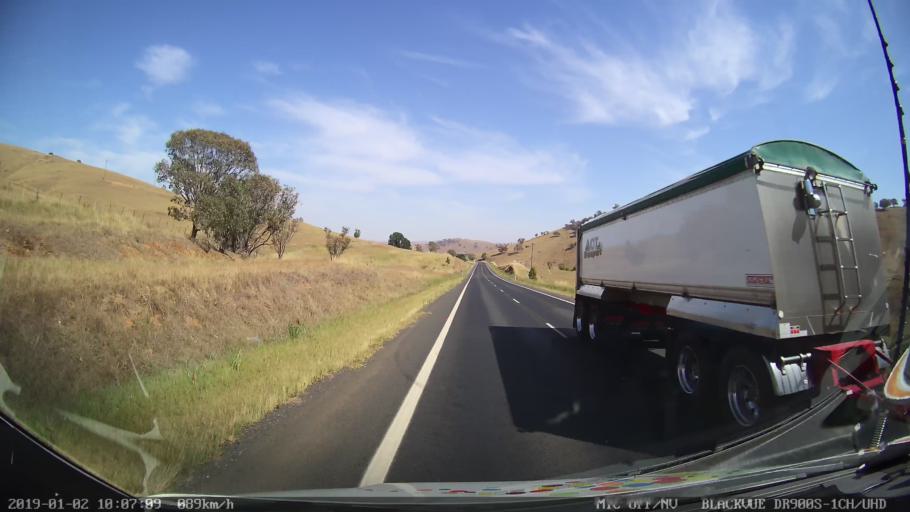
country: AU
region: New South Wales
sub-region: Gundagai
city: Gundagai
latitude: -35.1411
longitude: 148.1156
